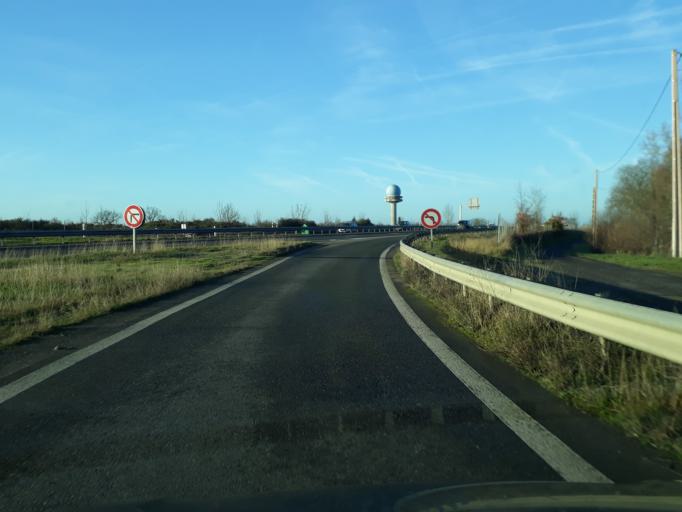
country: FR
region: Midi-Pyrenees
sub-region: Departement du Gers
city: Pujaudran
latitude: 43.5832
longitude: 1.1409
